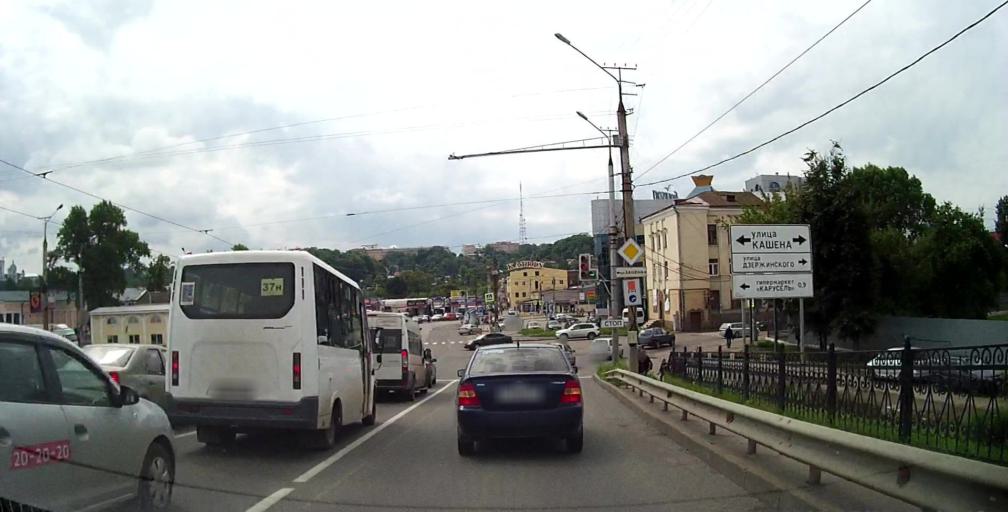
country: RU
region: Smolensk
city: Smolensk
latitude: 54.7960
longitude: 32.0433
